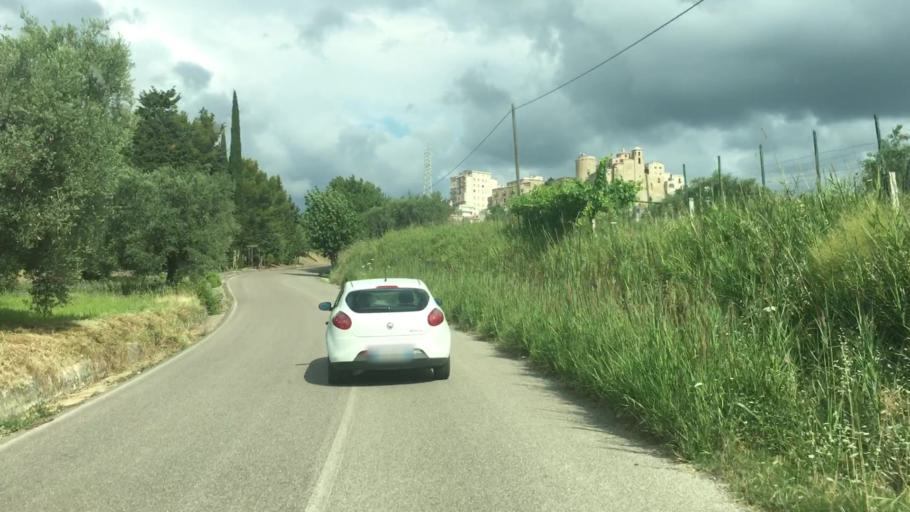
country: IT
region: Basilicate
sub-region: Provincia di Matera
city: San Mauro Forte
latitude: 40.4830
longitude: 16.2571
